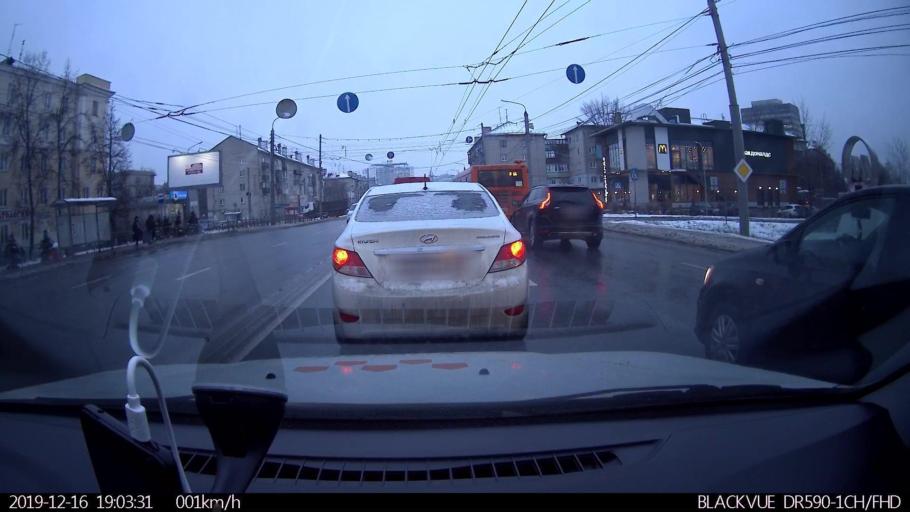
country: RU
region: Nizjnij Novgorod
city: Nizhniy Novgorod
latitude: 56.2974
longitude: 43.9371
